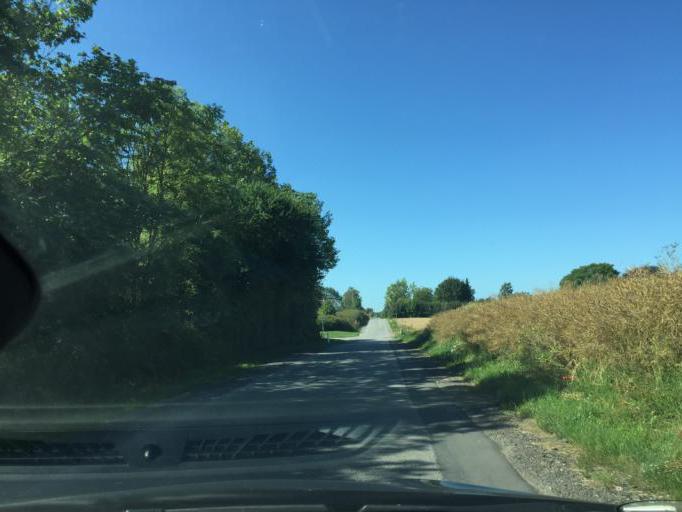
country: DK
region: South Denmark
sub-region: Nordfyns Kommune
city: Sonderso
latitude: 55.4792
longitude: 10.2670
